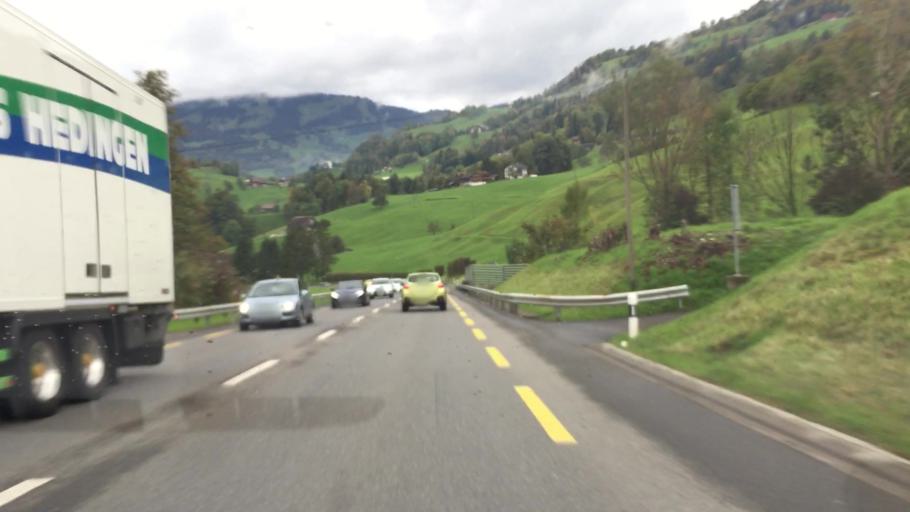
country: CH
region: Schwyz
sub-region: Bezirk Schwyz
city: Schwyz
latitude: 47.0328
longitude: 8.6413
